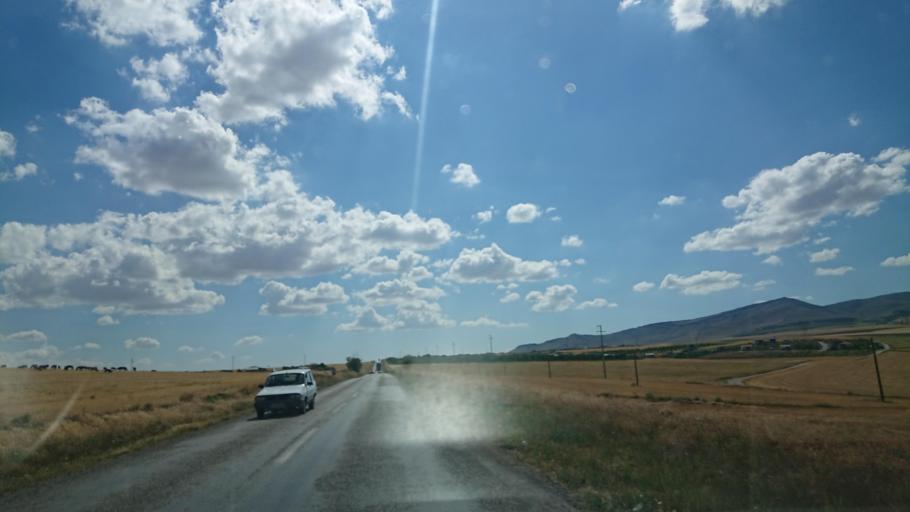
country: TR
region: Kirsehir
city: Kirsehir
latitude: 39.1480
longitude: 34.0954
